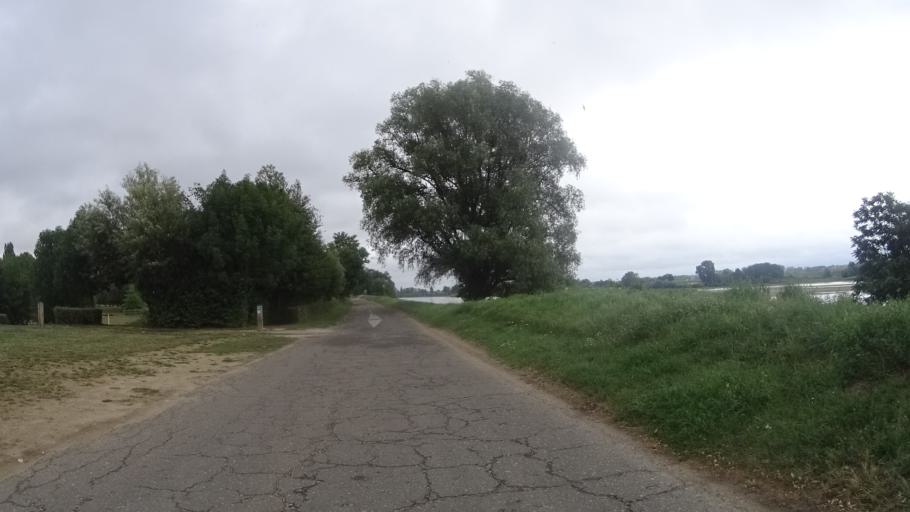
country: FR
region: Centre
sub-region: Departement du Loir-et-Cher
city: La Chaussee-Saint-Victor
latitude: 47.5971
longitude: 1.3577
